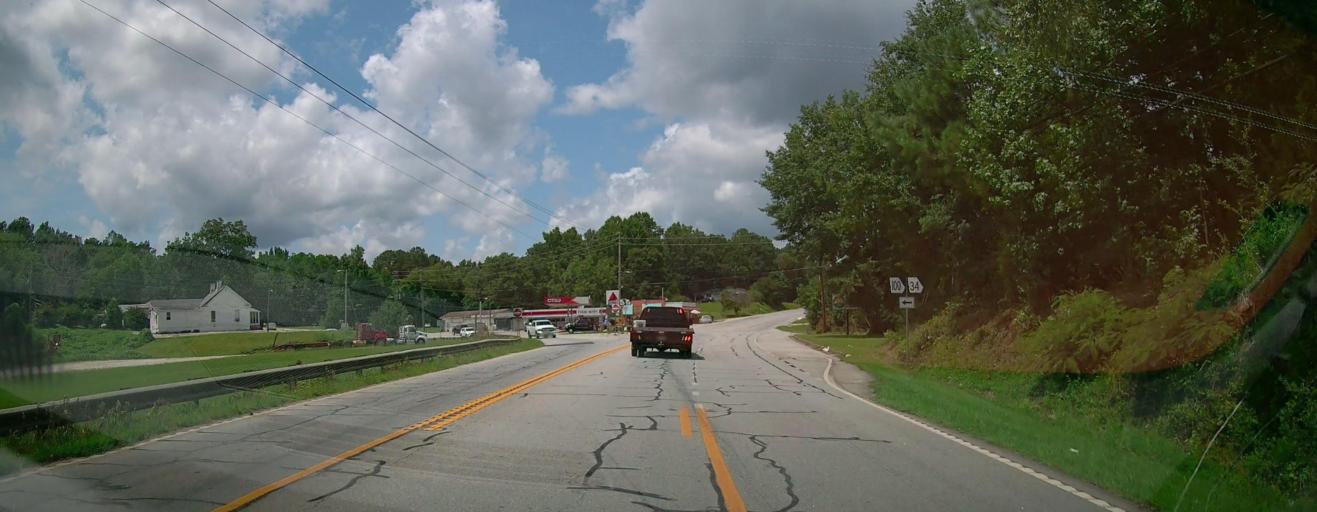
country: US
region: Georgia
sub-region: Heard County
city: Franklin
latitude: 33.2831
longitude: -85.1071
